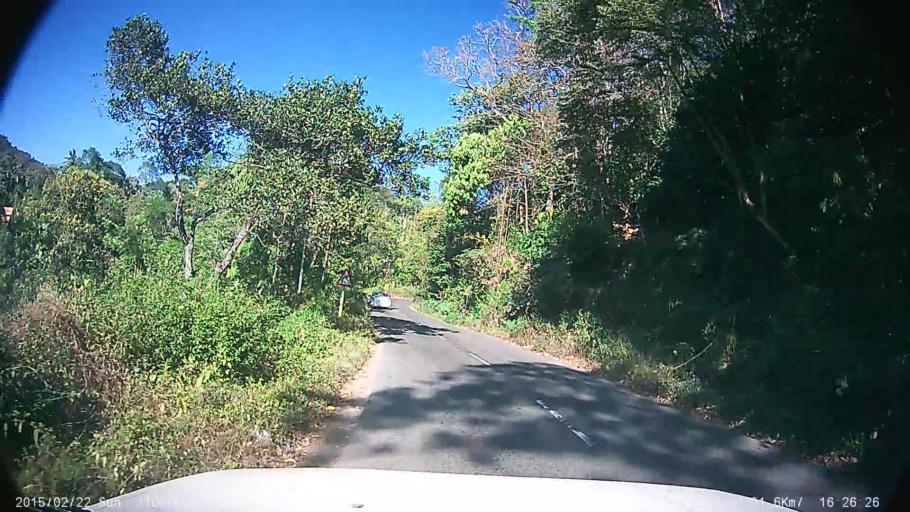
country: IN
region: Tamil Nadu
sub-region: Theni
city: Gudalur
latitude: 9.6024
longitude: 77.1362
